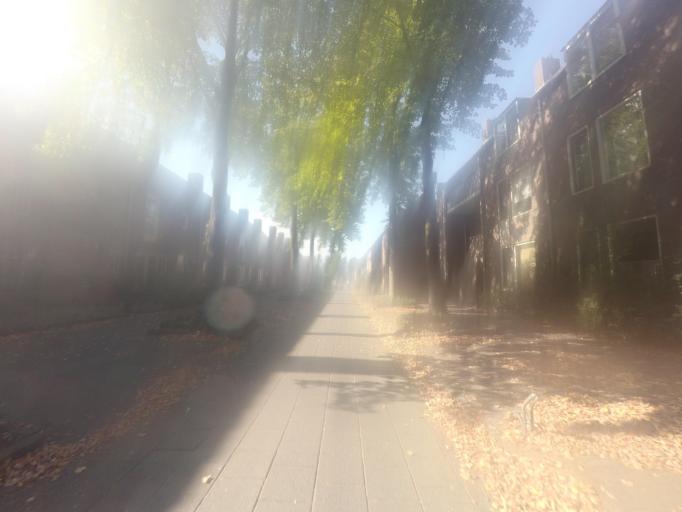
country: NL
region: North Brabant
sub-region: Gemeente Goirle
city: Goirle
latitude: 51.5283
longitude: 5.0488
